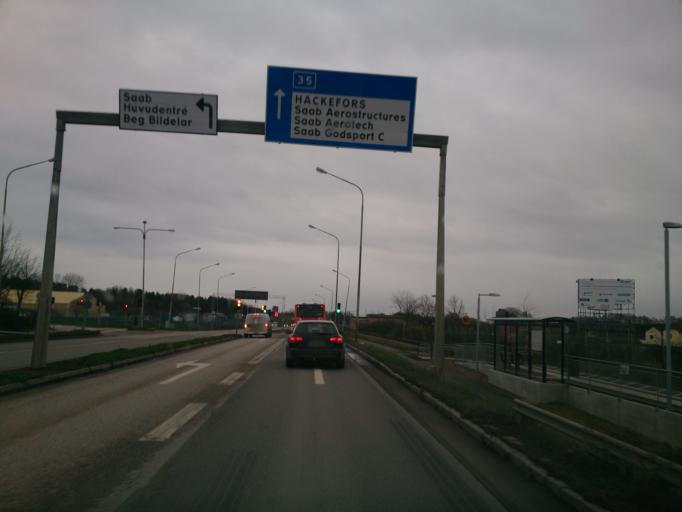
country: SE
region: OEstergoetland
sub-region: Linkopings Kommun
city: Linkoping
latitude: 58.4005
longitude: 15.6601
